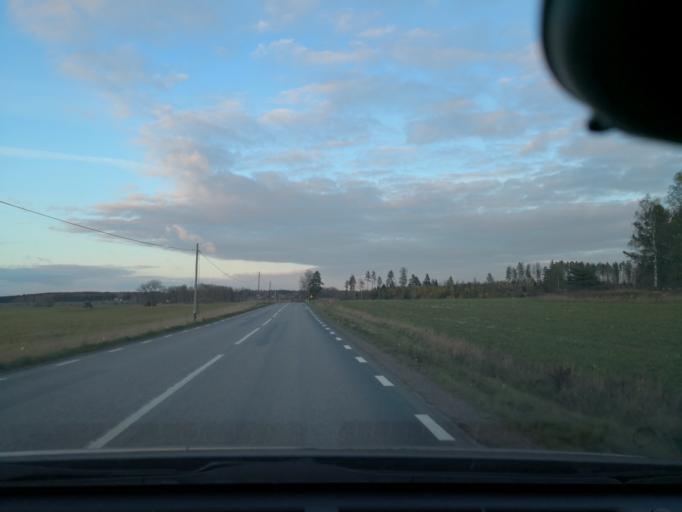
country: SE
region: Vaestmanland
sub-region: Vasteras
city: Tillberga
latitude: 59.6610
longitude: 16.6998
